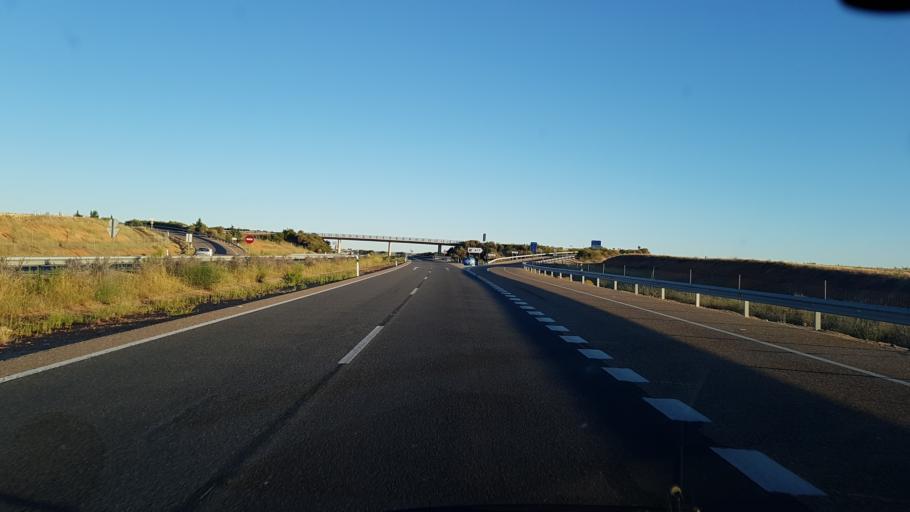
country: ES
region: Castille and Leon
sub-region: Provincia de Zamora
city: Morales de Toro
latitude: 41.5377
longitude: -5.2862
